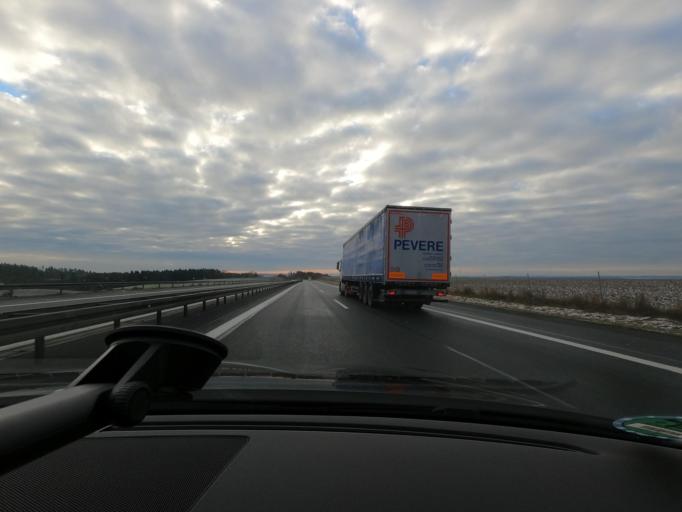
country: DE
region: Bavaria
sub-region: Upper Franconia
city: Meeder
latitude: 50.3331
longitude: 10.9375
